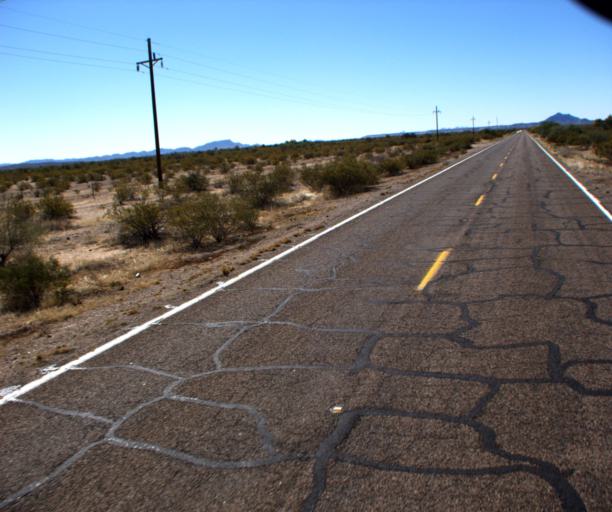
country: US
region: Arizona
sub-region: Pima County
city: Ajo
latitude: 32.4720
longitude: -112.8764
